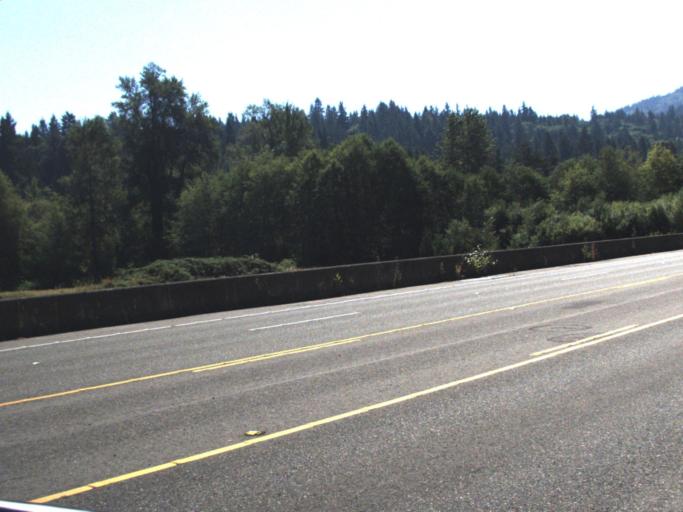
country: US
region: Washington
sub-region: King County
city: Issaquah
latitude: 47.5371
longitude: -122.0628
